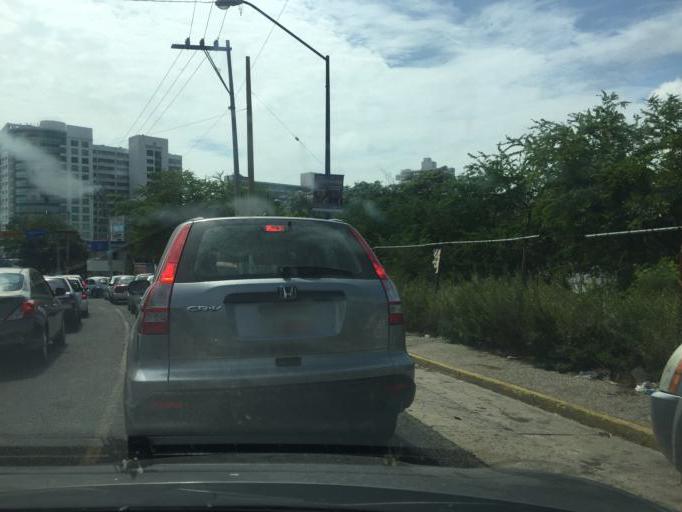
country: MX
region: Guerrero
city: Acapulco de Juarez
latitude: 16.8609
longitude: -99.8711
